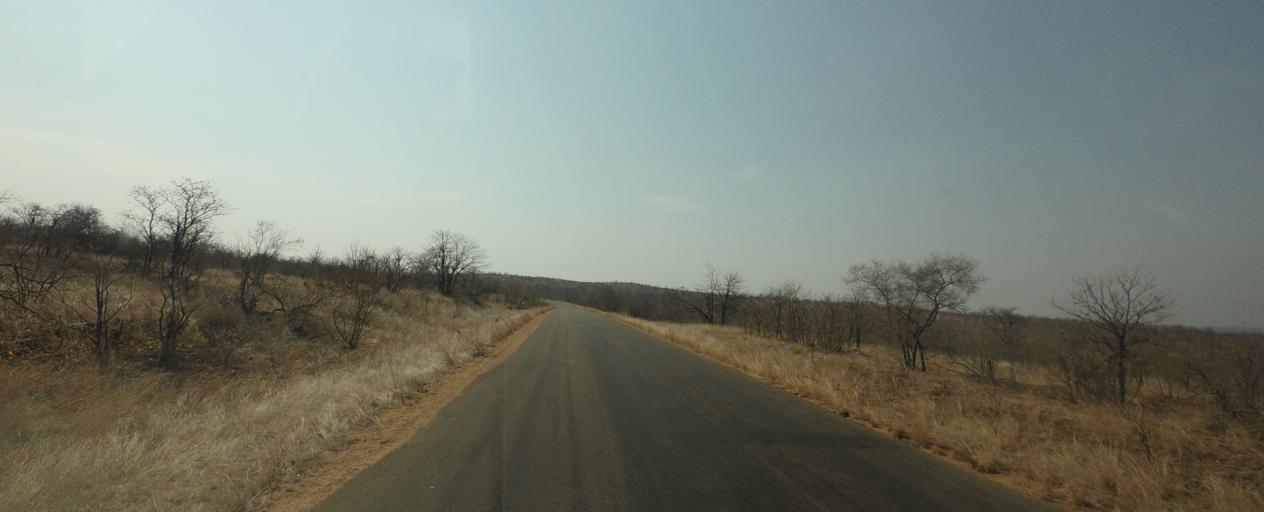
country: ZA
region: Limpopo
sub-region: Mopani District Municipality
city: Phalaborwa
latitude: -23.9735
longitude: 31.6352
